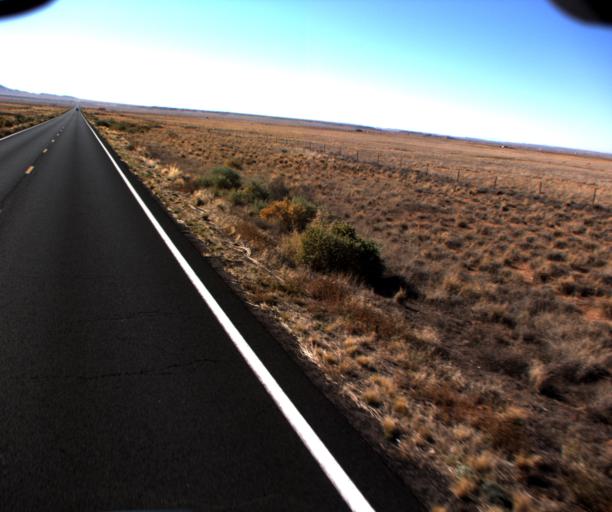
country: US
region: Arizona
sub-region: Navajo County
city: Dilkon
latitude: 35.3800
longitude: -110.4254
